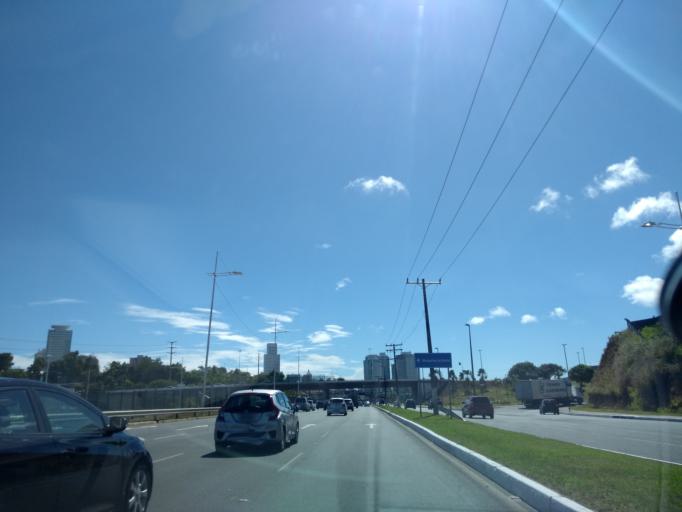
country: BR
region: Bahia
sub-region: Salvador
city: Salvador
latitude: -12.9725
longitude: -38.4483
